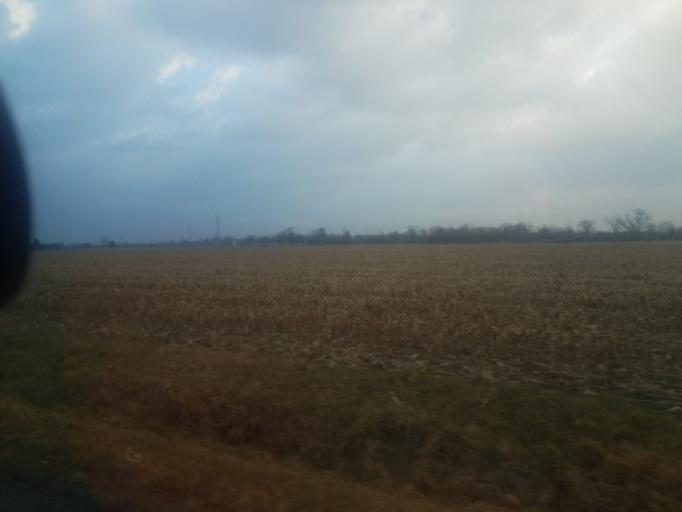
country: US
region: Ohio
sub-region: Marion County
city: Marion
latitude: 40.5979
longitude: -83.1689
